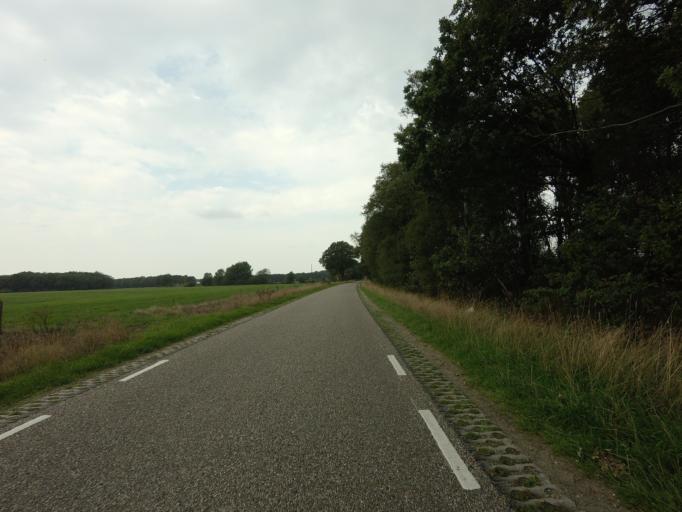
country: NL
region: Drenthe
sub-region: Gemeente Tynaarlo
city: Vries
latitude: 53.0429
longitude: 6.5970
